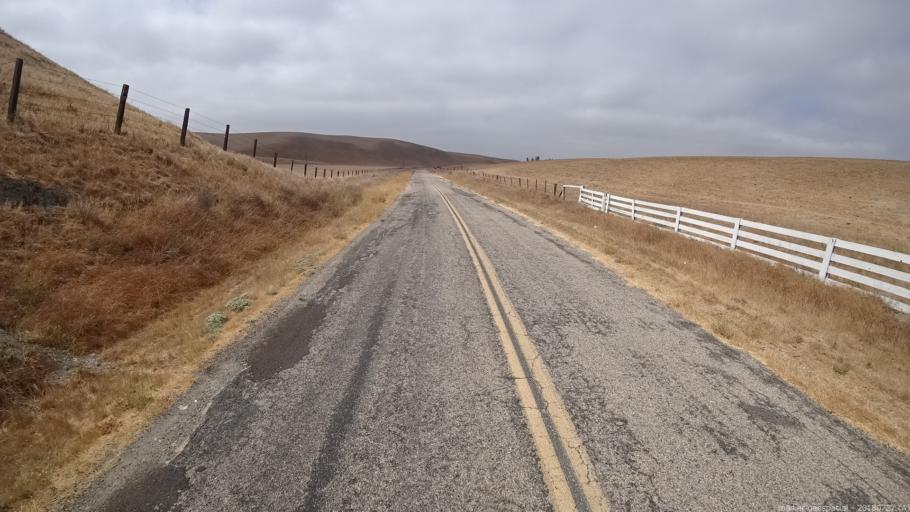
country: US
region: California
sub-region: Monterey County
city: King City
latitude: 36.2266
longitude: -121.0644
